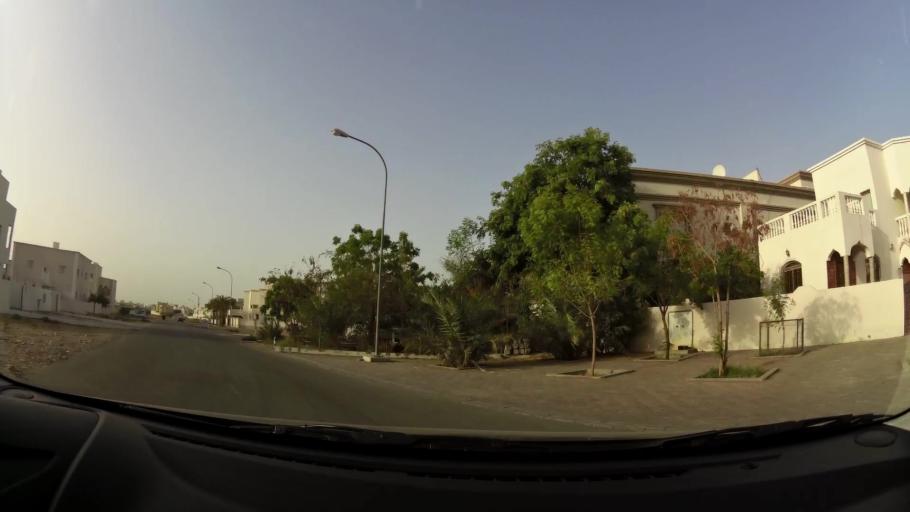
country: OM
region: Muhafazat Masqat
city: Bawshar
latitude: 23.5323
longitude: 58.3527
